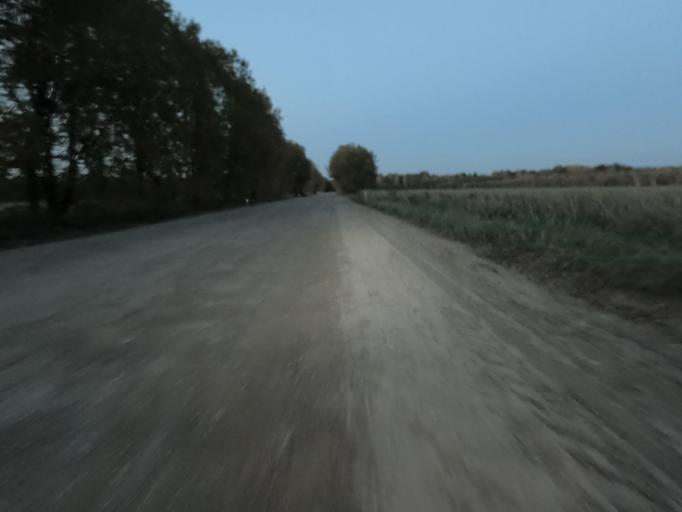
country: RU
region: Leningrad
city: Lyuban'
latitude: 59.1839
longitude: 31.2422
